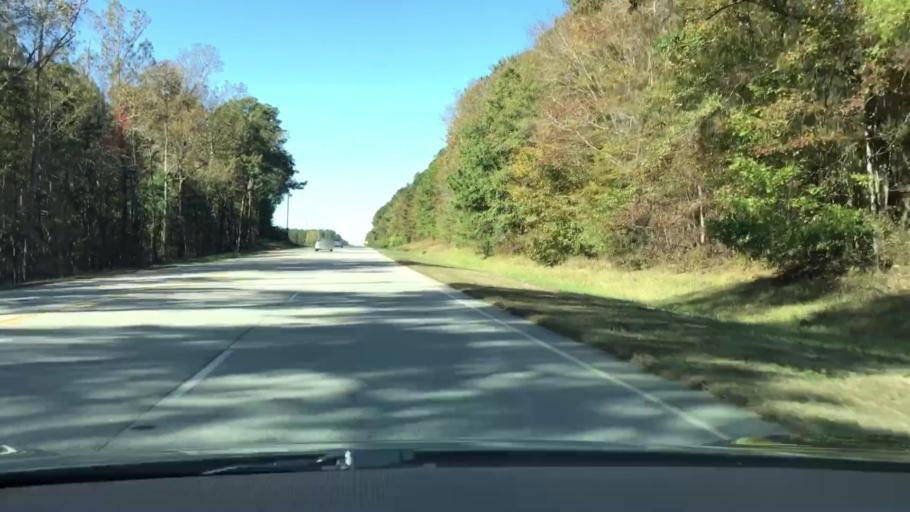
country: US
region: Georgia
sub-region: Warren County
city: Firing Range
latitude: 33.4795
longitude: -82.7460
